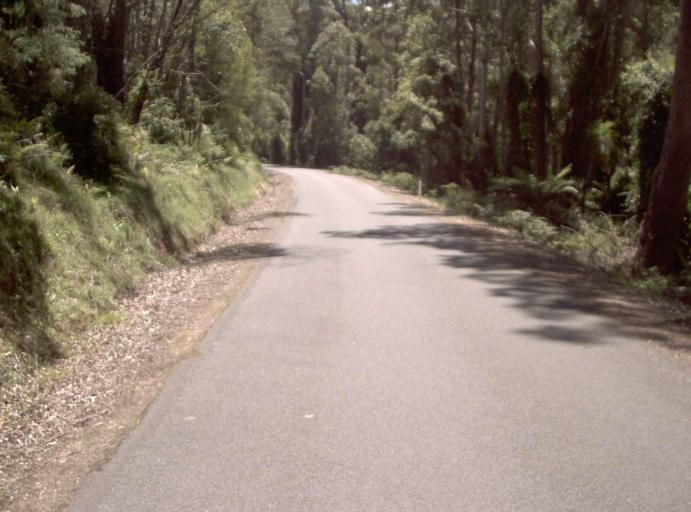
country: AU
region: New South Wales
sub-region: Bombala
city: Bombala
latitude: -37.4847
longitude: 148.9295
